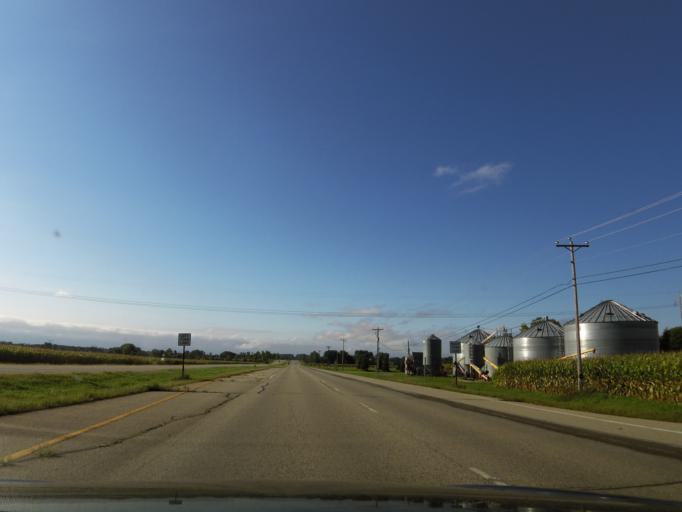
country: US
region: Minnesota
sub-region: Washington County
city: Lake Elmo
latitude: 44.9577
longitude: -92.8627
